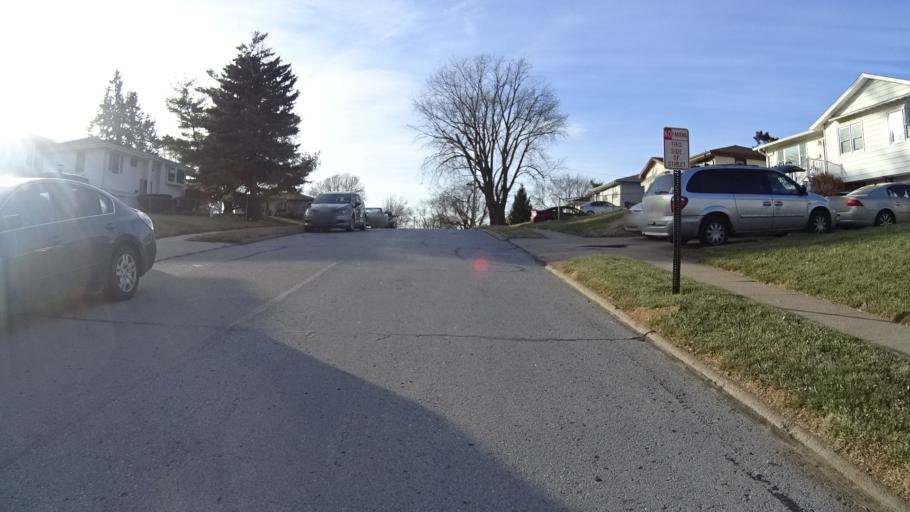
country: US
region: Nebraska
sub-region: Sarpy County
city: La Vista
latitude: 41.1888
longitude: -95.9949
